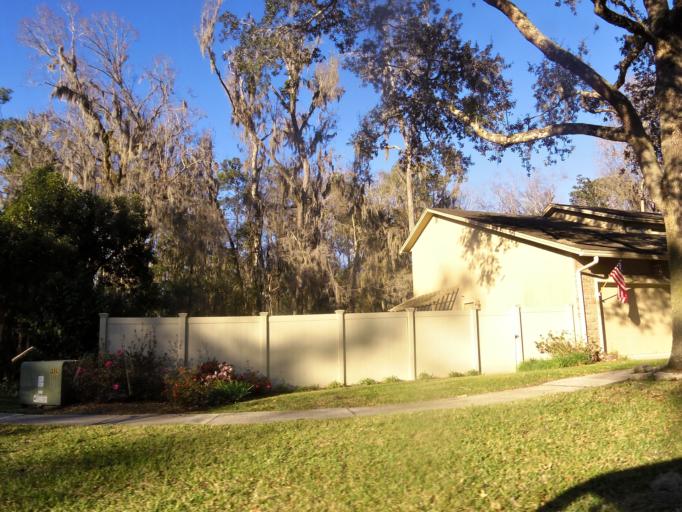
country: US
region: Florida
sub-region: Saint Johns County
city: Fruit Cove
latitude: 30.2144
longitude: -81.6066
